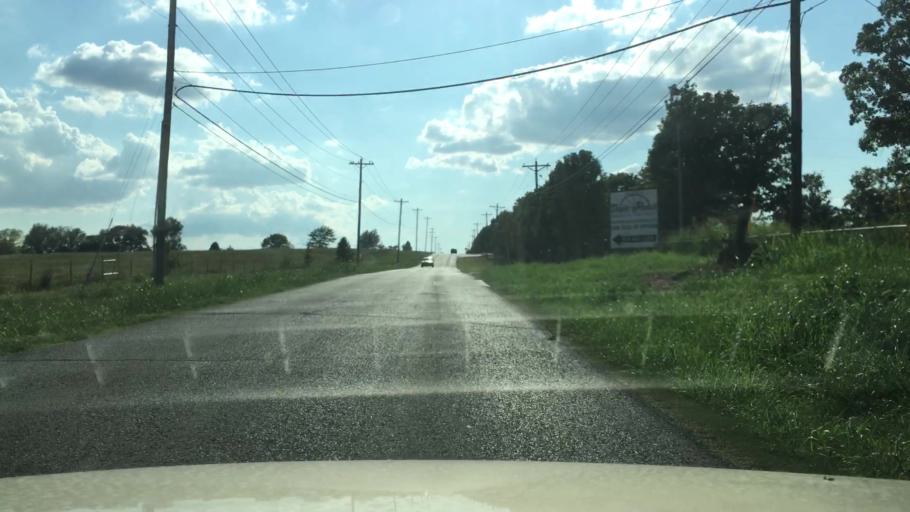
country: US
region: Oklahoma
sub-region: Cherokee County
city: Tahlequah
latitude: 35.9299
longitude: -94.9786
